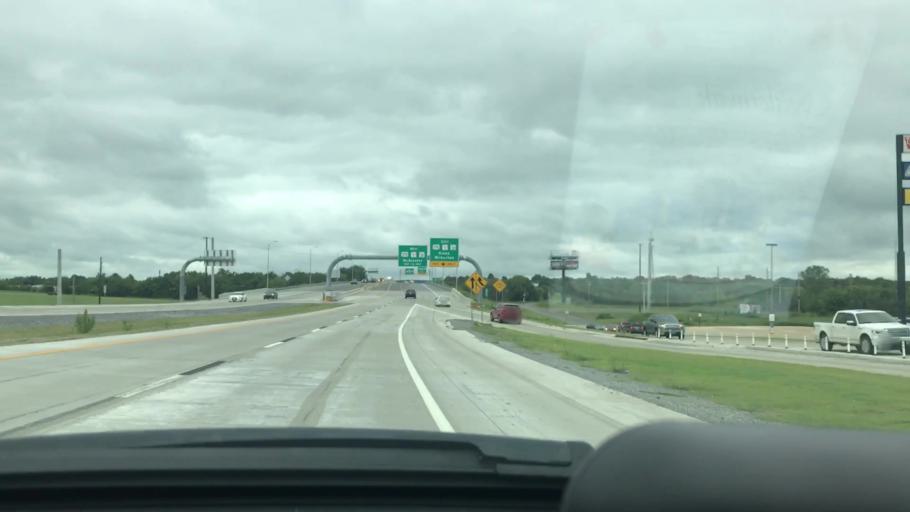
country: US
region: Oklahoma
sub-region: Pittsburg County
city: McAlester
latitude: 34.9207
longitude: -95.7444
